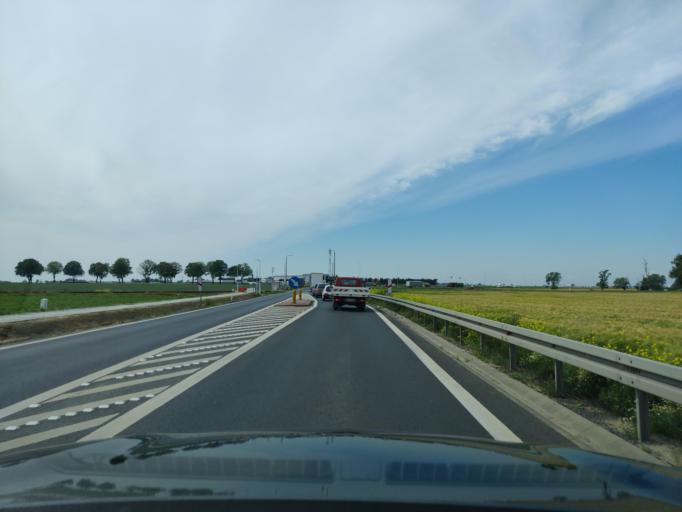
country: PL
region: Greater Poland Voivodeship
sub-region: Powiat grodziski
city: Granowo
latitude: 52.2232
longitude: 16.5850
